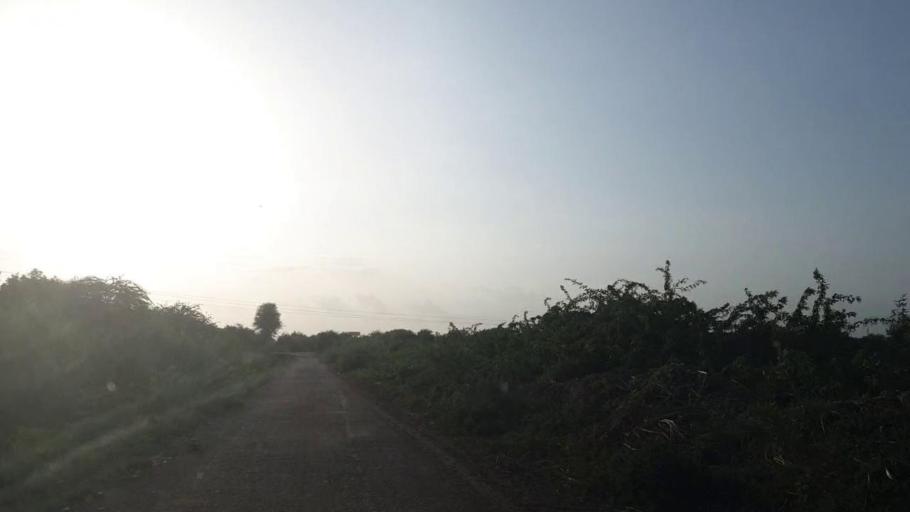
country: PK
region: Sindh
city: Kadhan
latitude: 24.6320
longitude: 69.1174
